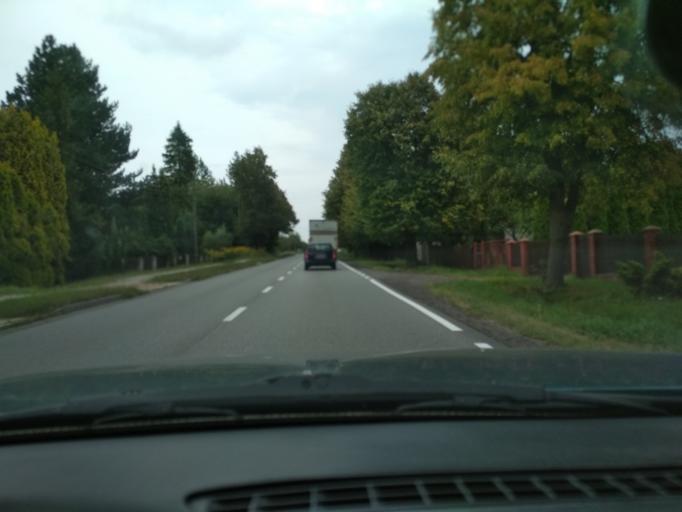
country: PL
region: Silesian Voivodeship
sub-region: Powiat zawiercianski
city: Wysoka
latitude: 50.4429
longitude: 19.3587
